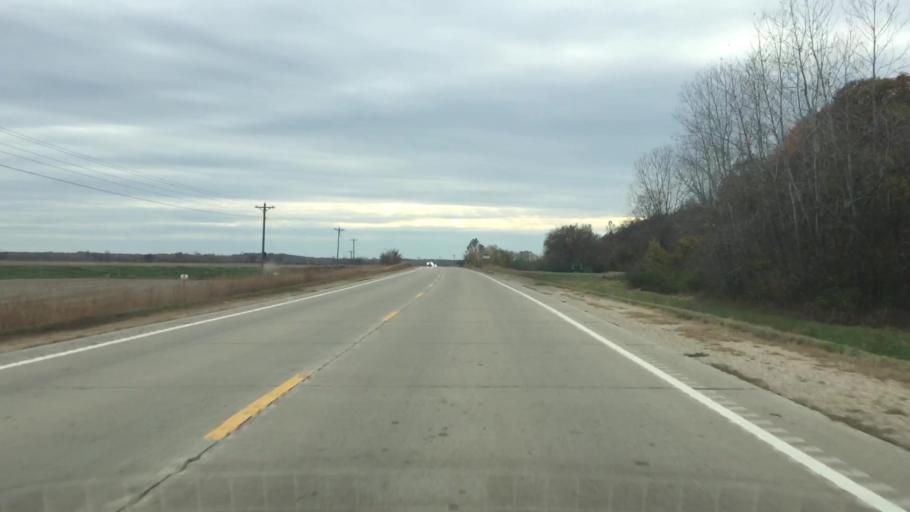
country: US
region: Missouri
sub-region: Callaway County
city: Holts Summit
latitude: 38.5898
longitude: -92.0254
